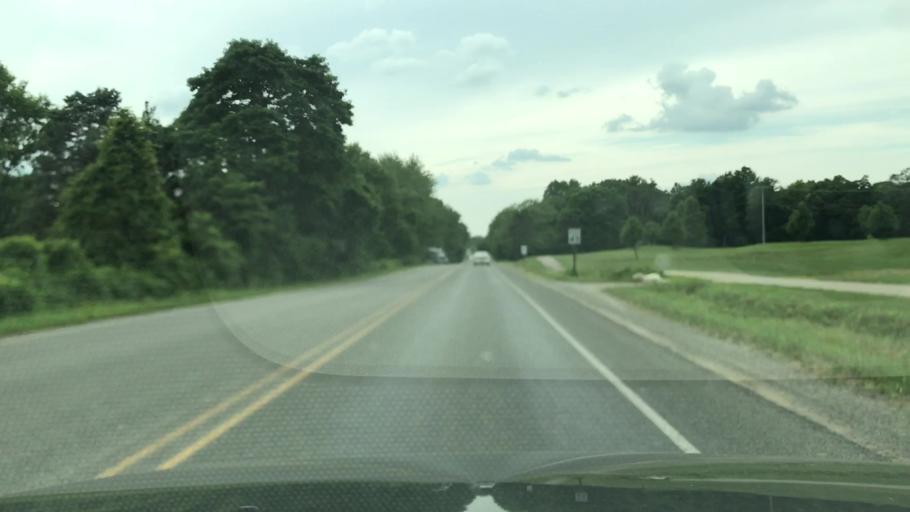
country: US
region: Michigan
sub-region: Kent County
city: East Grand Rapids
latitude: 42.9845
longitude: -85.5618
